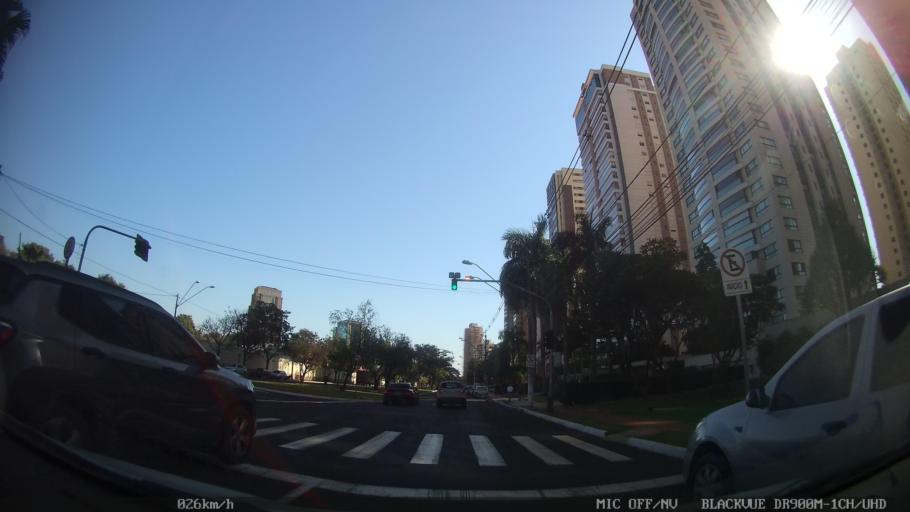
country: BR
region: Sao Paulo
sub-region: Ribeirao Preto
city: Ribeirao Preto
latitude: -21.2087
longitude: -47.8071
